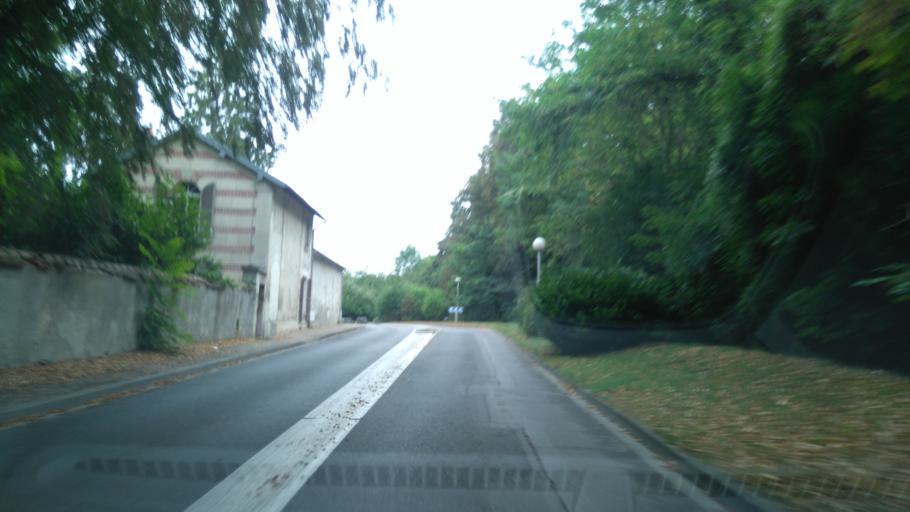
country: FR
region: Picardie
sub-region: Departement de l'Oise
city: Gouvieux
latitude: 49.1870
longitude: 2.4026
